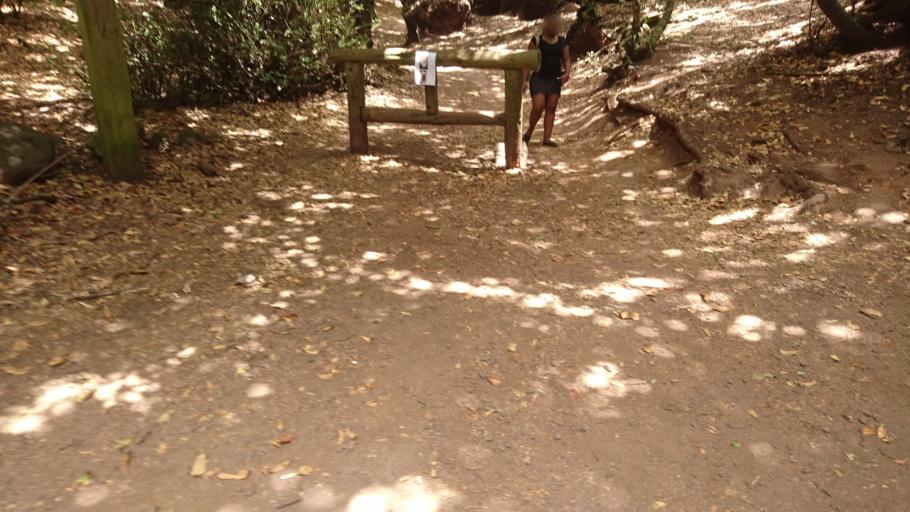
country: ES
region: Canary Islands
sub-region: Provincia de Santa Cruz de Tenerife
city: Tegueste
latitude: 28.5265
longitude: -16.2818
